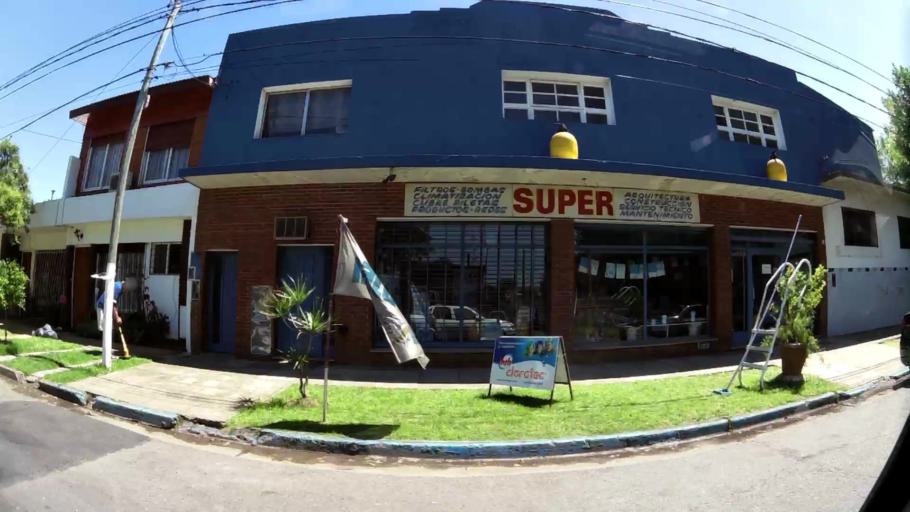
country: AR
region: Buenos Aires
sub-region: Partido de Vicente Lopez
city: Olivos
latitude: -34.5104
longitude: -58.5166
